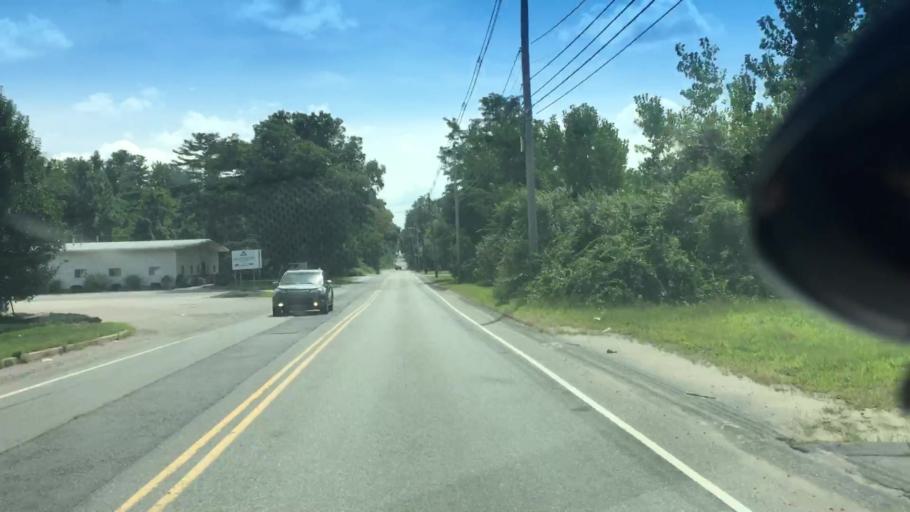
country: US
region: Massachusetts
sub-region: Norfolk County
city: Stoughton
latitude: 42.1380
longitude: -71.0765
